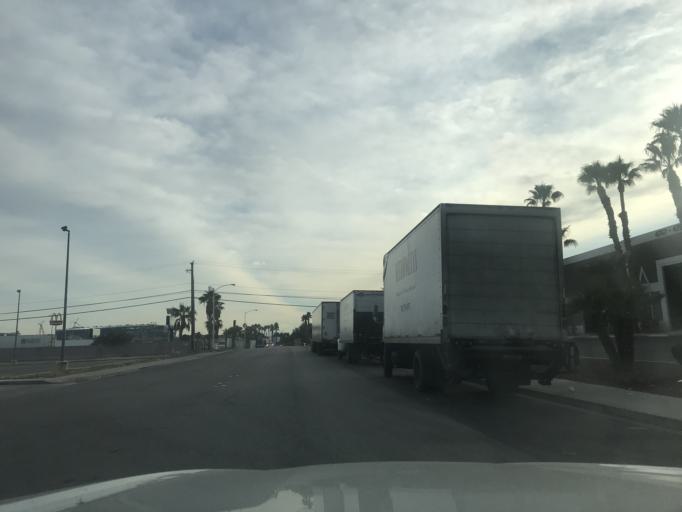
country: US
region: Nevada
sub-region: Clark County
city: Paradise
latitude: 36.1036
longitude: -115.1877
